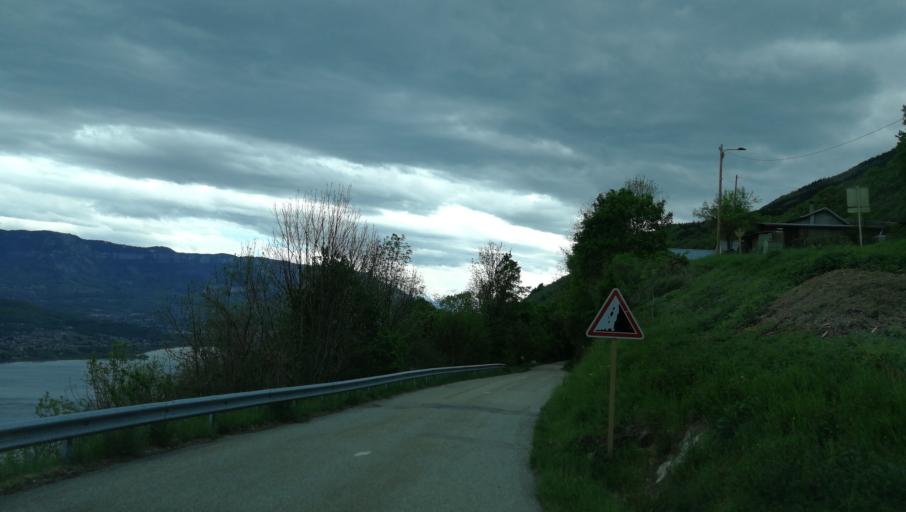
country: FR
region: Rhone-Alpes
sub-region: Departement de la Savoie
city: Chatillon
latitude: 45.7486
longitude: 5.8319
